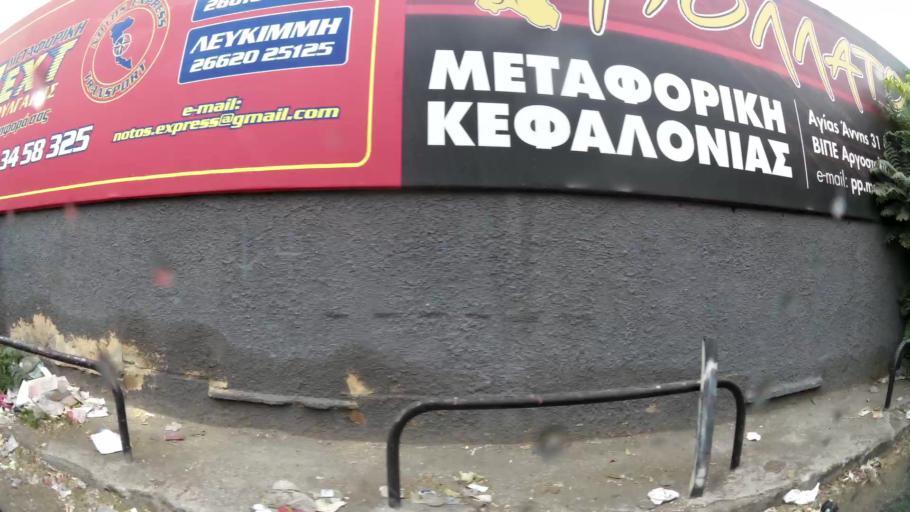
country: GR
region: Attica
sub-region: Nomarchia Athinas
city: Aigaleo
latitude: 37.9812
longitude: 23.6898
